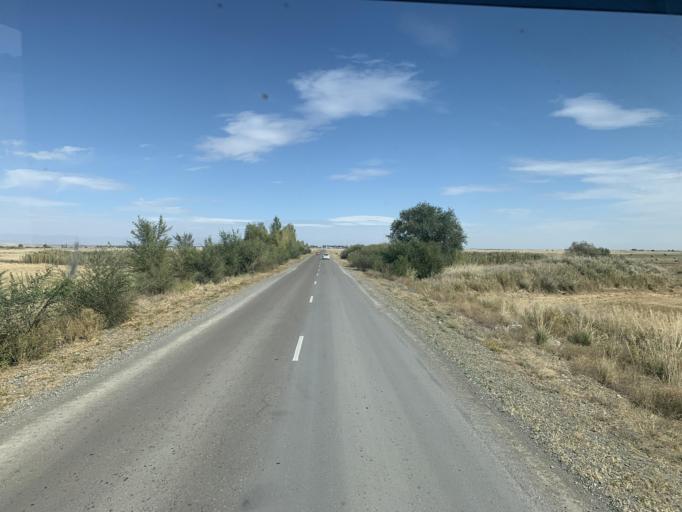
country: CN
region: Xinjiang Uygur Zizhiqu
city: Tacheng
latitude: 46.6643
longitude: 82.7526
